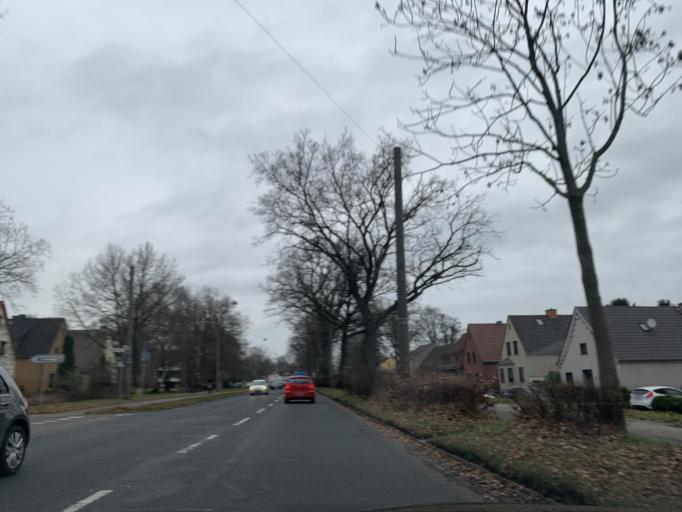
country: DE
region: Lower Saxony
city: Ritterhude
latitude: 53.1483
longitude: 8.7111
